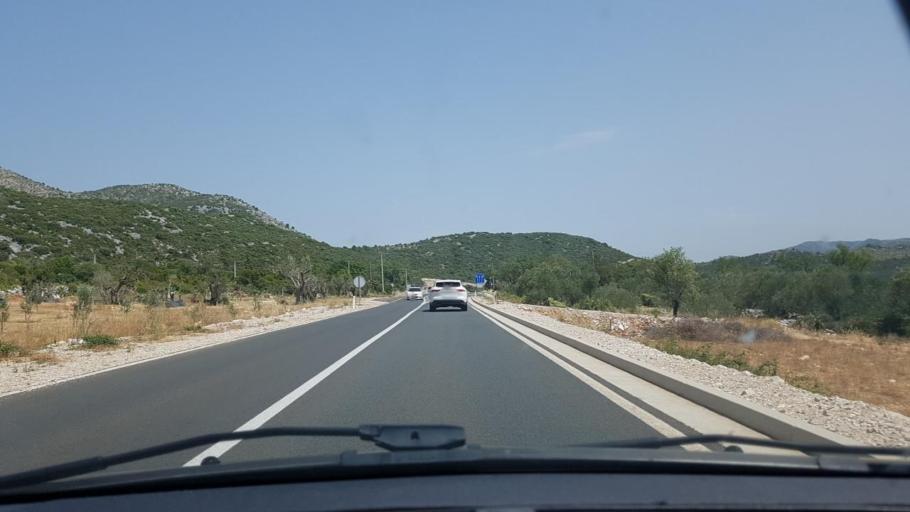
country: HR
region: Dubrovacko-Neretvanska
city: Ston
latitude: 42.9527
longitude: 17.7478
